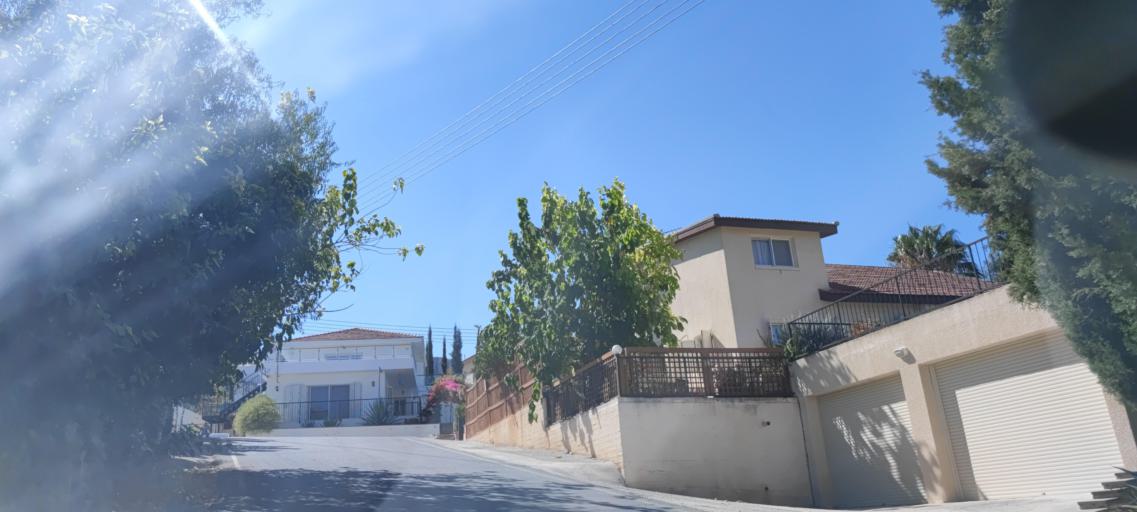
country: CY
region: Limassol
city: Mouttagiaka
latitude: 34.7529
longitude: 33.1017
